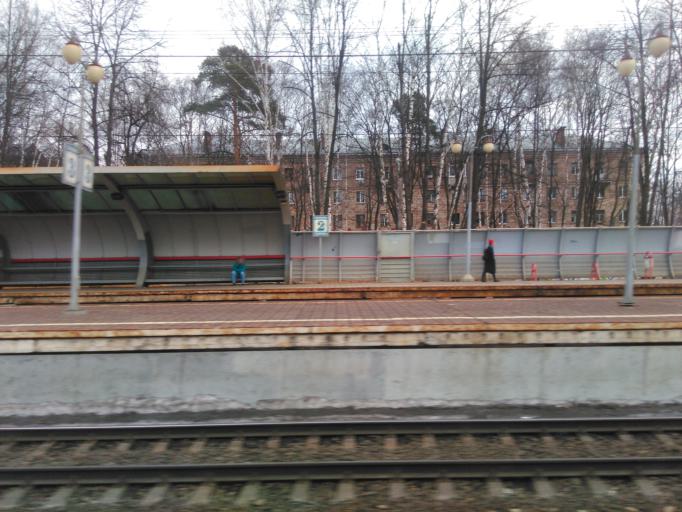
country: RU
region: Moscow
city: Yaroslavskiy
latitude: 55.8892
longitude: 37.7247
